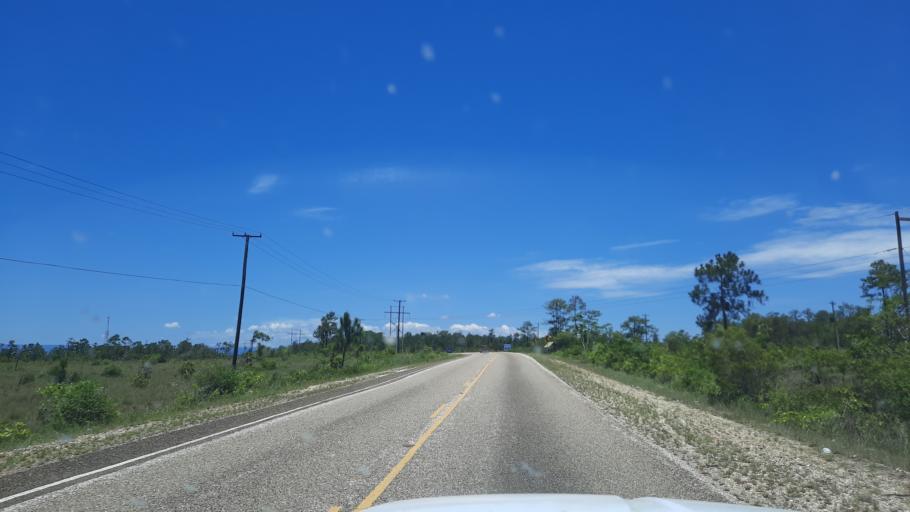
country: BZ
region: Cayo
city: Belmopan
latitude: 17.3569
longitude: -88.5493
